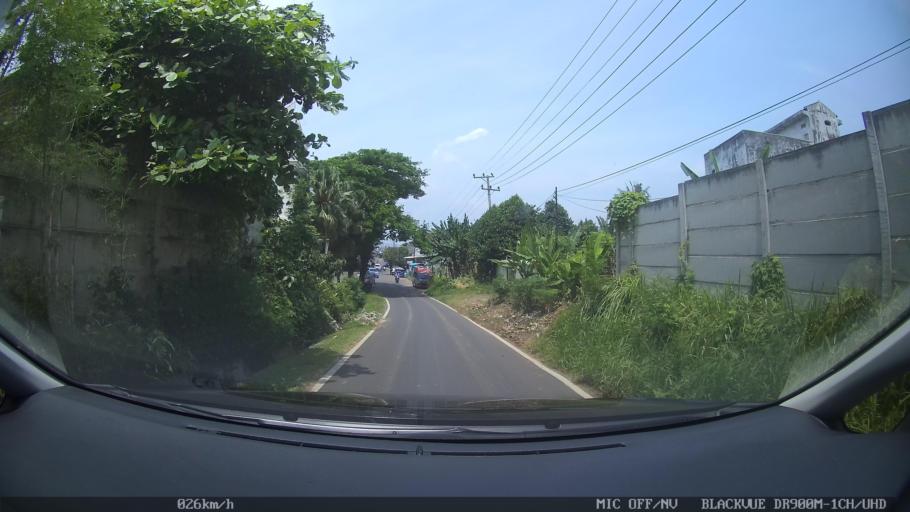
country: ID
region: Lampung
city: Bandarlampung
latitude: -5.4462
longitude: 105.2482
